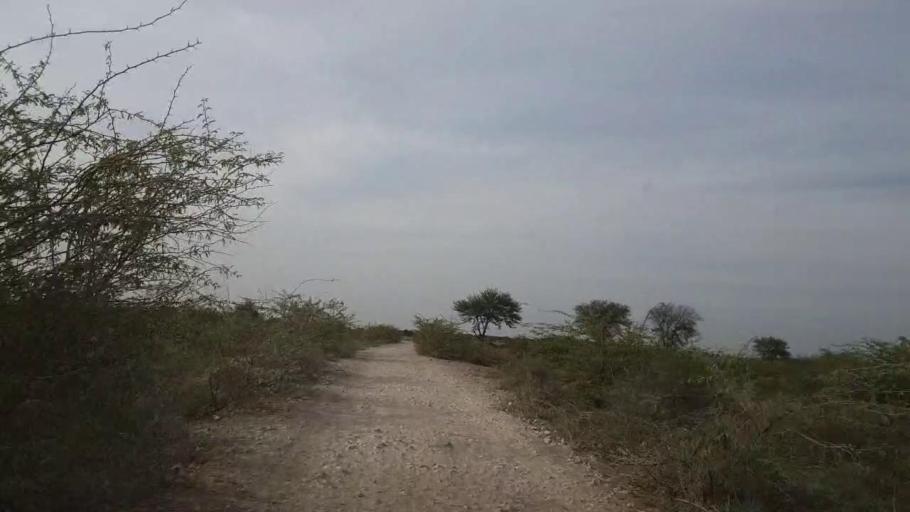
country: PK
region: Sindh
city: Nabisar
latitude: 24.9991
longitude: 69.5431
